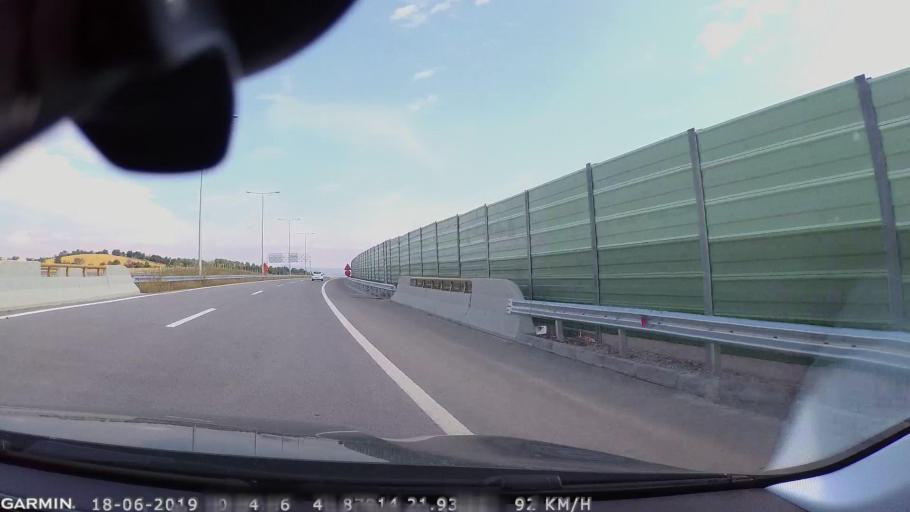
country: MK
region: Sveti Nikole
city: Sveti Nikole
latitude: 41.8795
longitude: 21.9363
